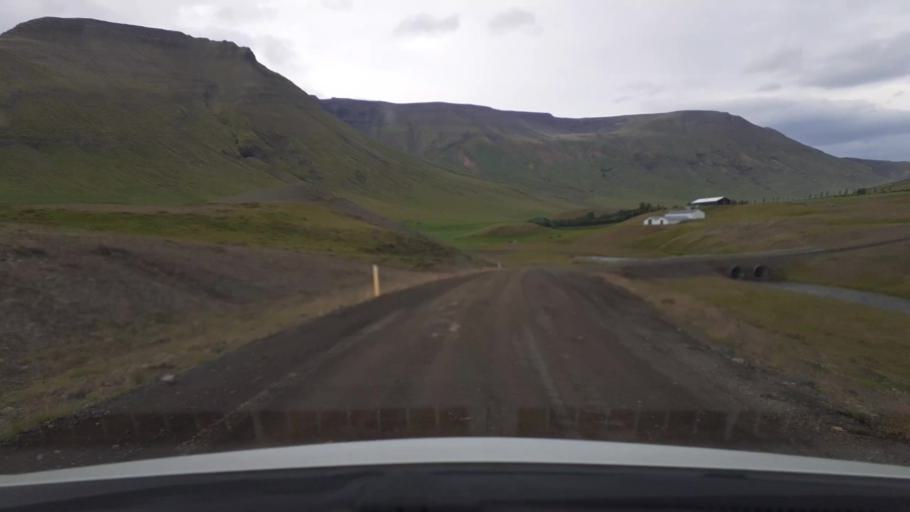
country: IS
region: Capital Region
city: Mosfellsbaer
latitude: 64.2955
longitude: -21.6578
